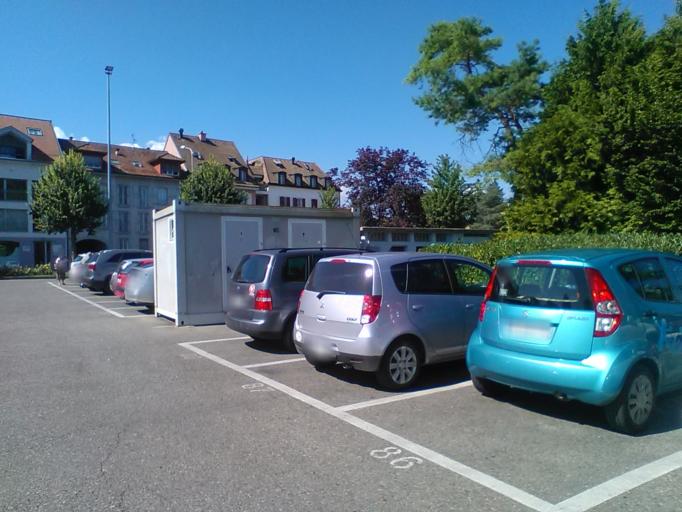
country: CH
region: Vaud
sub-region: Nyon District
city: Nyon
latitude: 46.3842
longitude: 6.2457
